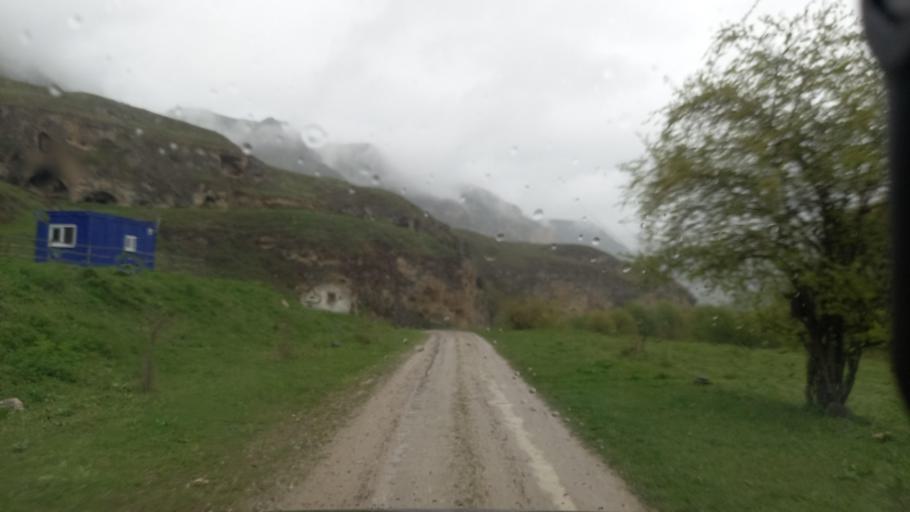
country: RU
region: Kabardino-Balkariya
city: Bylym
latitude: 43.5912
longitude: 43.0262
